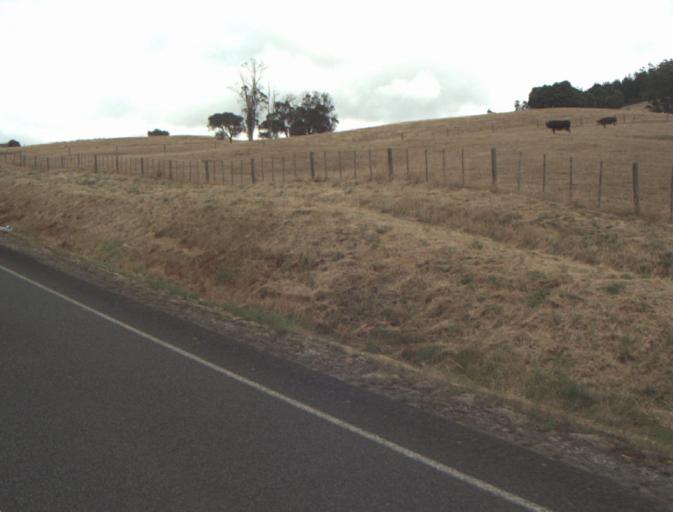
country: AU
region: Tasmania
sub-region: Launceston
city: Mayfield
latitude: -41.2809
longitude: 147.2197
